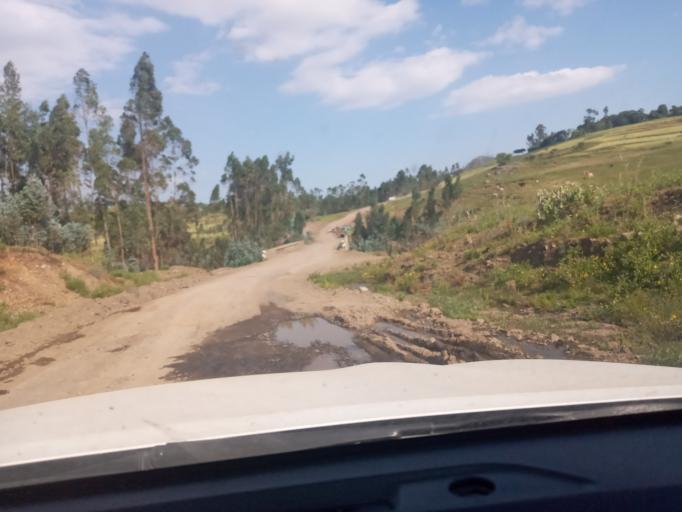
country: ET
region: Amhara
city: Were Ilu
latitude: 10.6142
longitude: 39.0456
